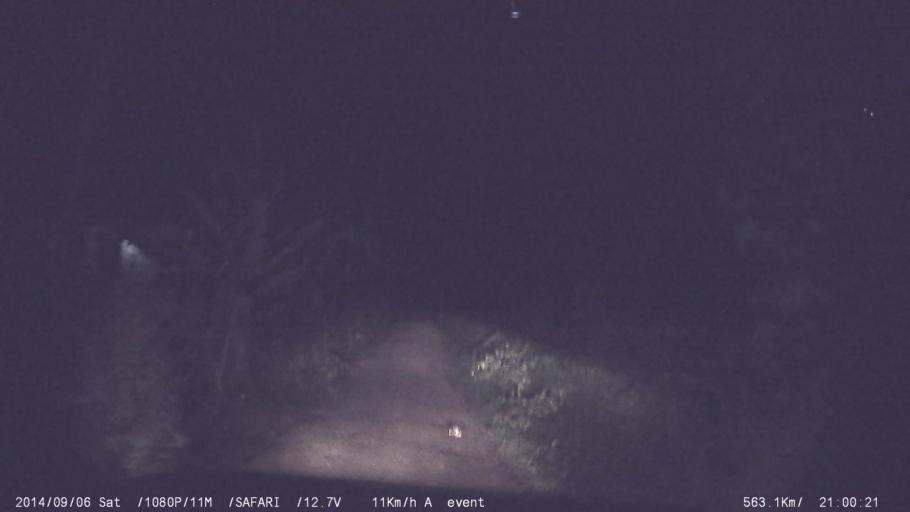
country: IN
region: Kerala
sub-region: Kottayam
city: Palackattumala
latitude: 9.7885
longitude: 76.5640
